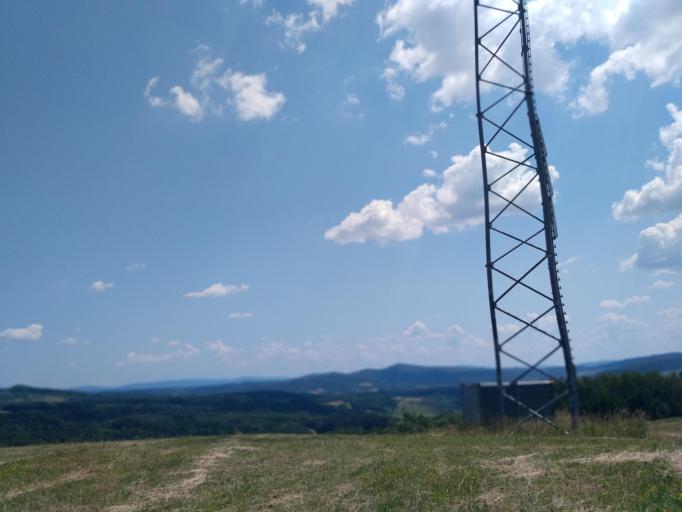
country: PL
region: Subcarpathian Voivodeship
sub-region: Powiat sanocki
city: Czaszyn
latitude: 49.4733
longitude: 22.1938
